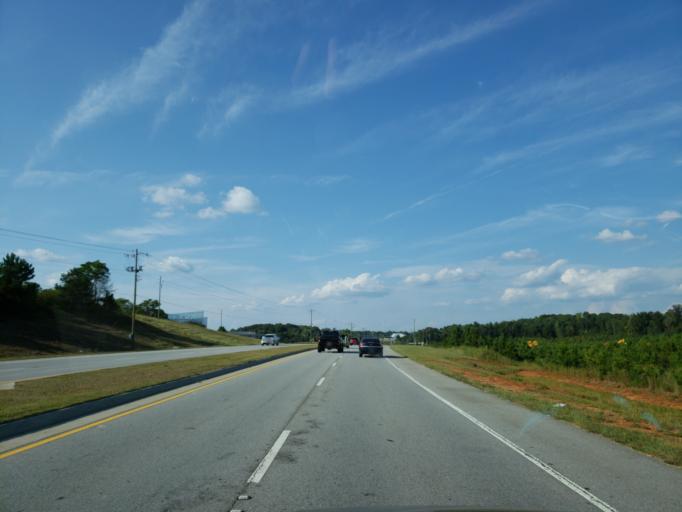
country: US
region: Georgia
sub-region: Paulding County
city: Hiram
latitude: 33.8969
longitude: -84.7796
